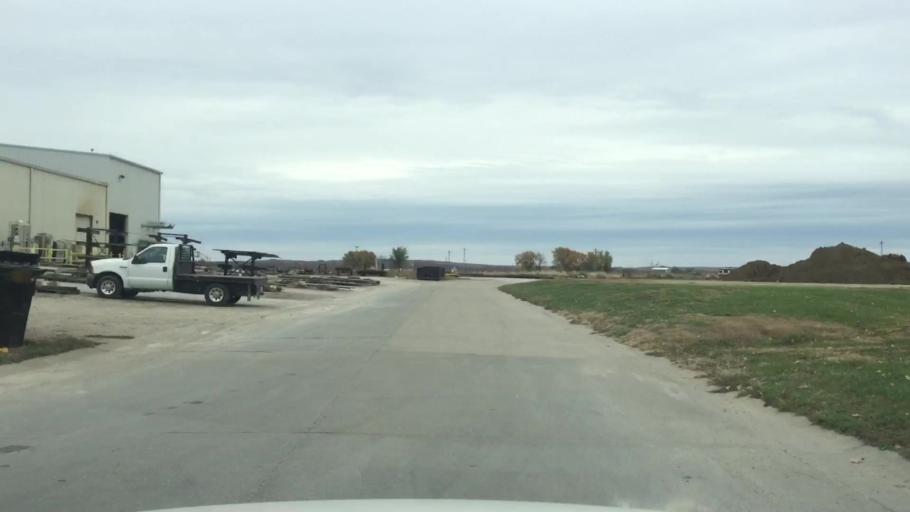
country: US
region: Kansas
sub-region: Pottawatomie County
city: Wamego
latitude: 39.2064
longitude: -96.2901
